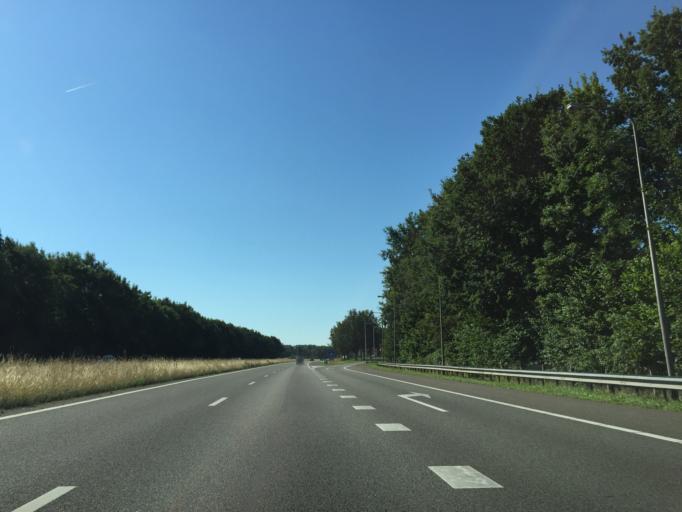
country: NL
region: Limburg
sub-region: Eijsden-Margraten
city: Eijsden
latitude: 50.7889
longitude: 5.7276
